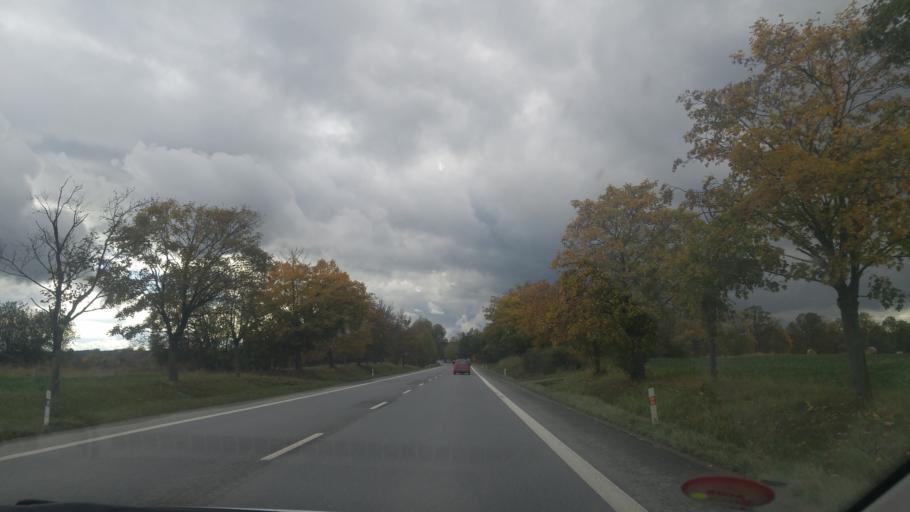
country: CZ
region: Jihocesky
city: Sevetin
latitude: 49.1217
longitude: 14.5956
